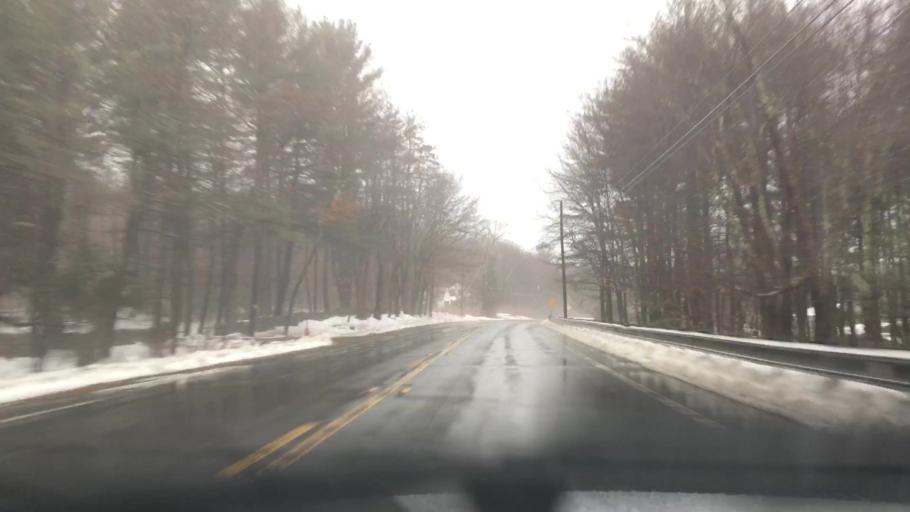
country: US
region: Massachusetts
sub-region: Hampshire County
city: Pelham
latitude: 42.3386
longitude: -72.4027
